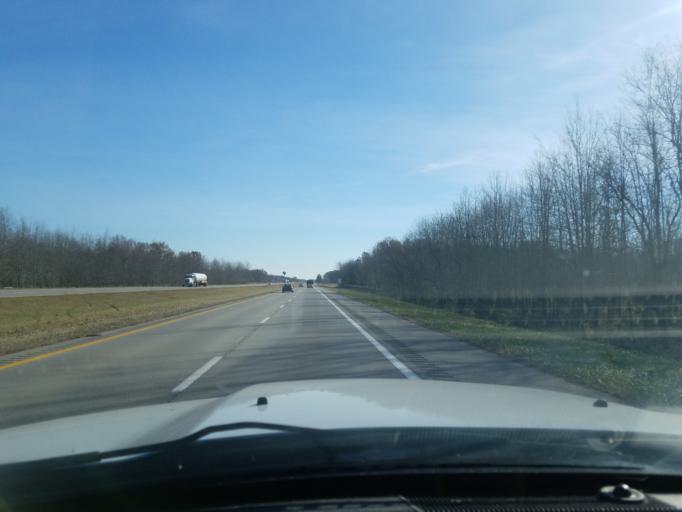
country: US
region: Ohio
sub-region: Brown County
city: Mount Orab
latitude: 39.0504
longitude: -83.9582
